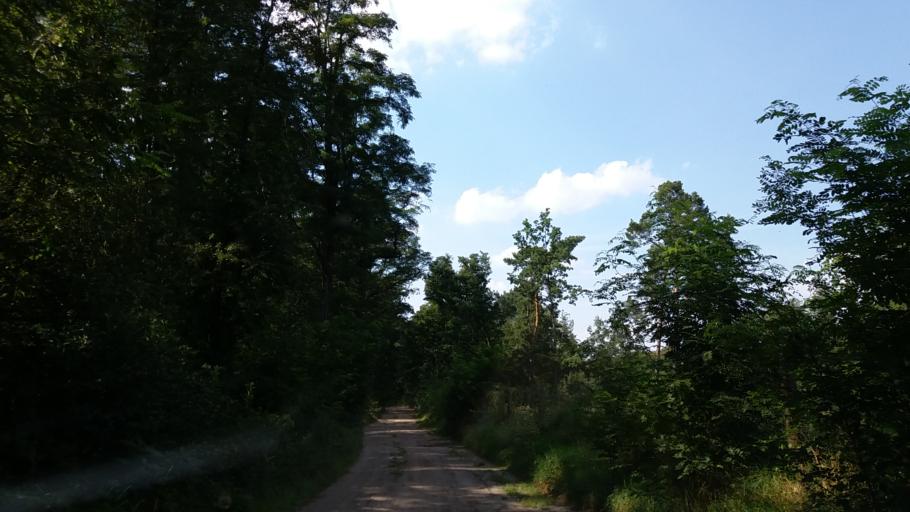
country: PL
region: West Pomeranian Voivodeship
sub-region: Powiat choszczenski
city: Choszczno
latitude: 53.1000
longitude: 15.4204
